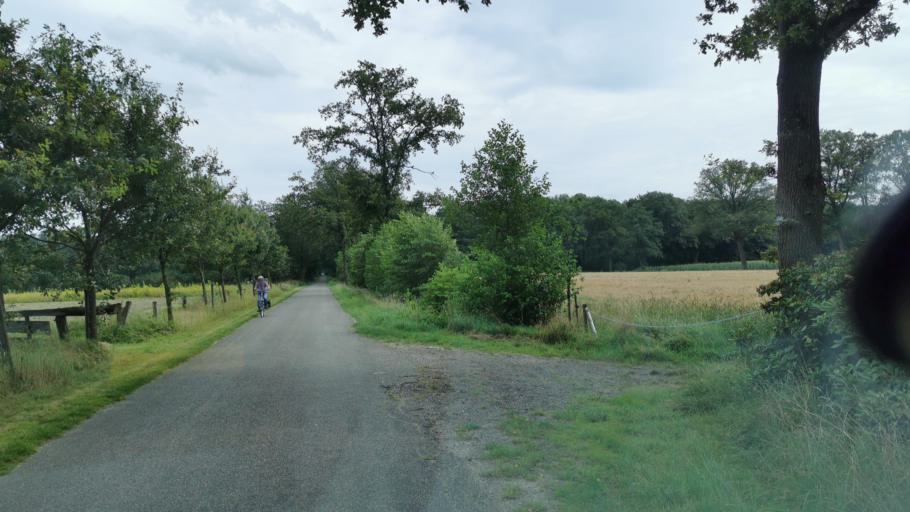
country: NL
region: Overijssel
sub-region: Gemeente Losser
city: Losser
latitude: 52.2432
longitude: 6.9614
